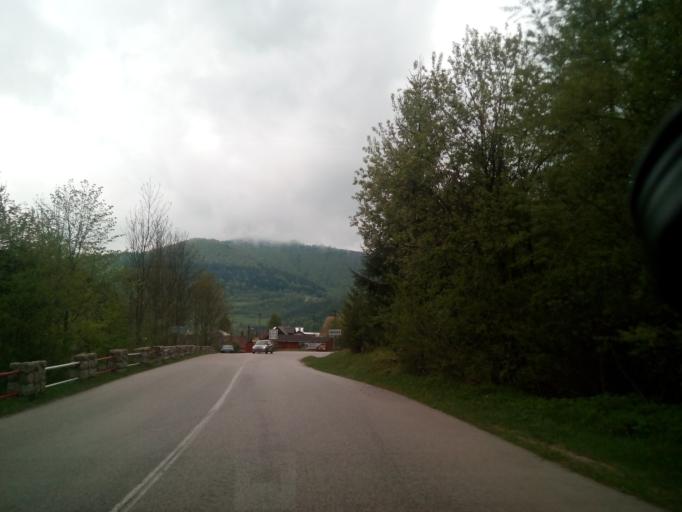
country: SK
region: Zilinsky
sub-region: Okres Zilina
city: Terchova
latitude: 49.2500
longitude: 19.0383
